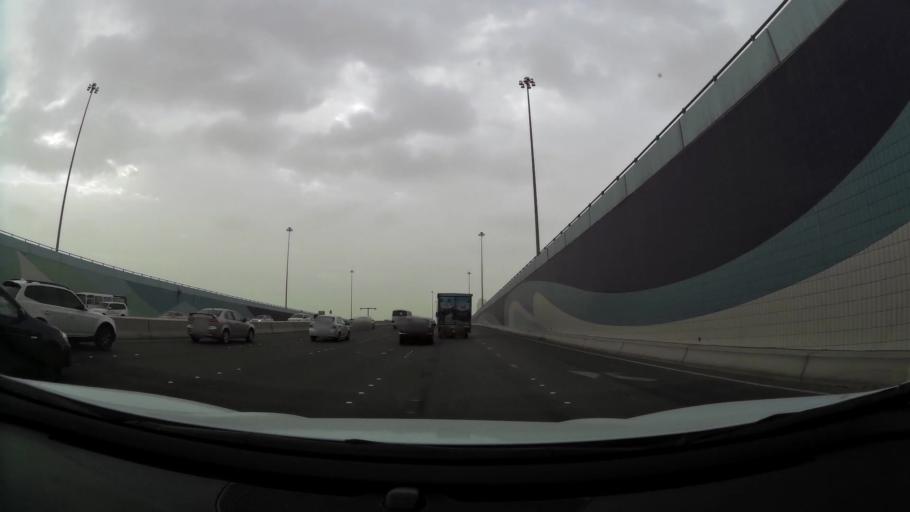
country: AE
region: Abu Dhabi
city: Abu Dhabi
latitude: 24.4711
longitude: 54.3928
